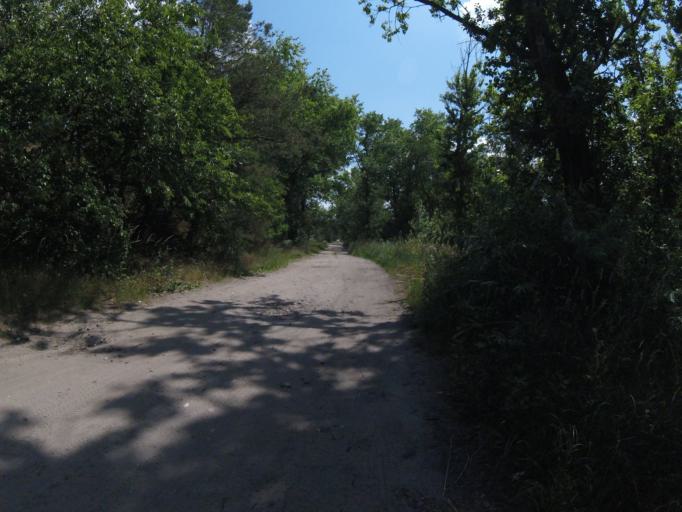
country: DE
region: Brandenburg
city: Bestensee
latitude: 52.2823
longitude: 13.6748
